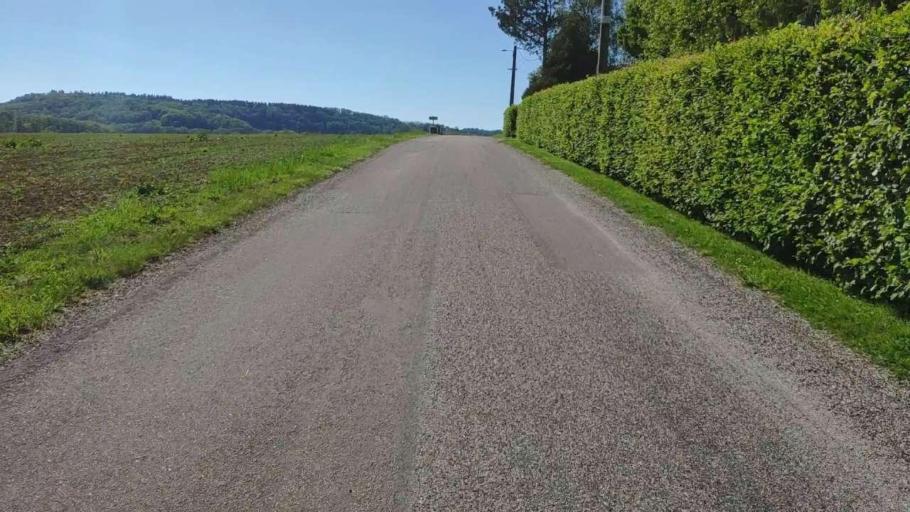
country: FR
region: Franche-Comte
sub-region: Departement du Jura
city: Perrigny
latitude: 46.7169
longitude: 5.5745
